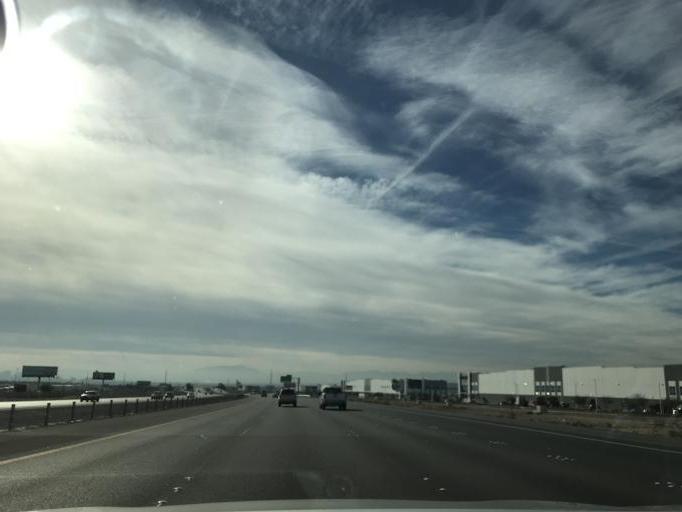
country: US
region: Nevada
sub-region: Clark County
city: Nellis Air Force Base
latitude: 36.2664
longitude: -115.0709
